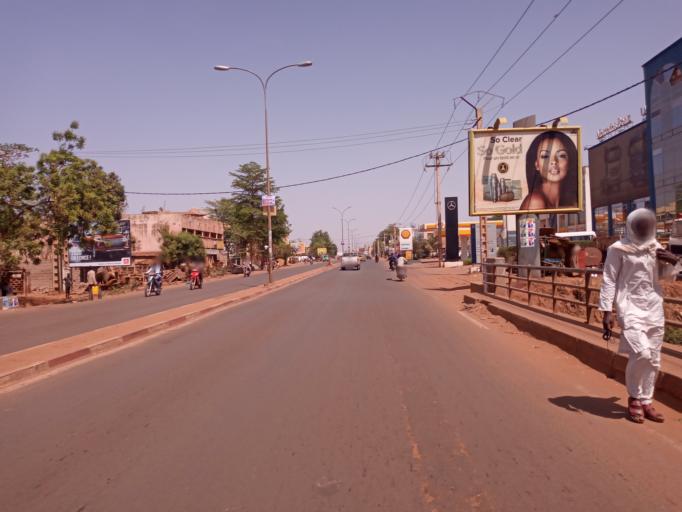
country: ML
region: Bamako
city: Bamako
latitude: 12.6632
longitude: -7.9484
